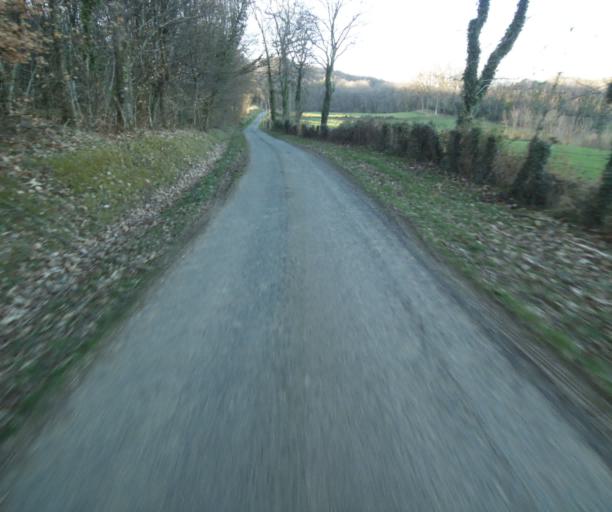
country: FR
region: Limousin
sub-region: Departement de la Correze
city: Seilhac
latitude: 45.3456
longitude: 1.7224
